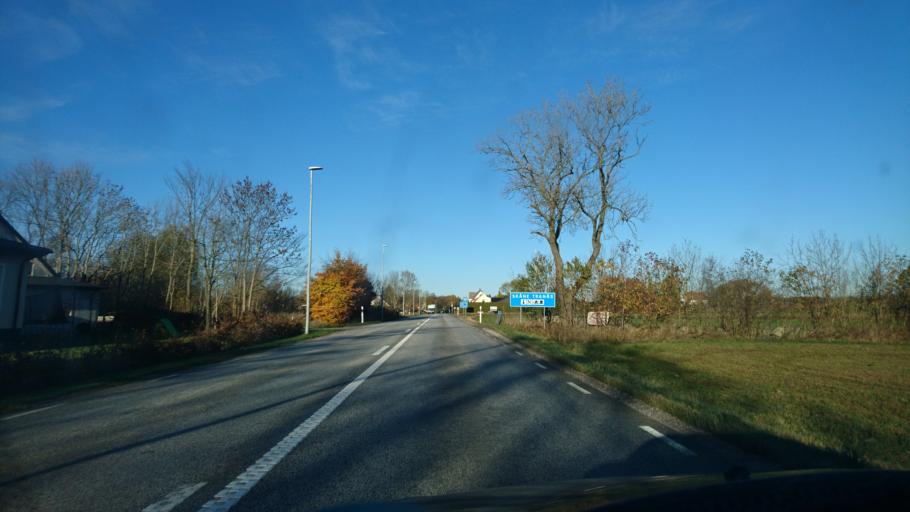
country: SE
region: Skane
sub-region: Tomelilla Kommun
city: Tomelilla
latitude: 55.6107
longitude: 13.9947
